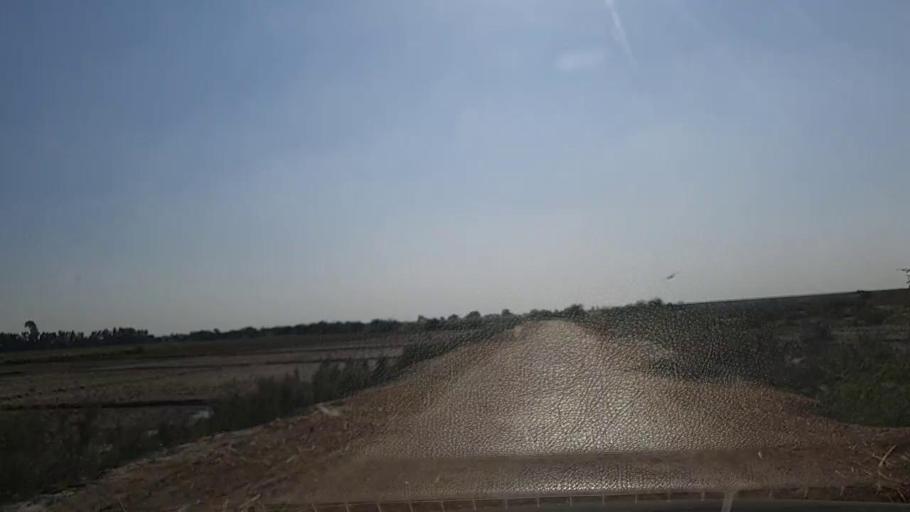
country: PK
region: Sindh
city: Daro Mehar
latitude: 24.7601
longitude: 68.0632
